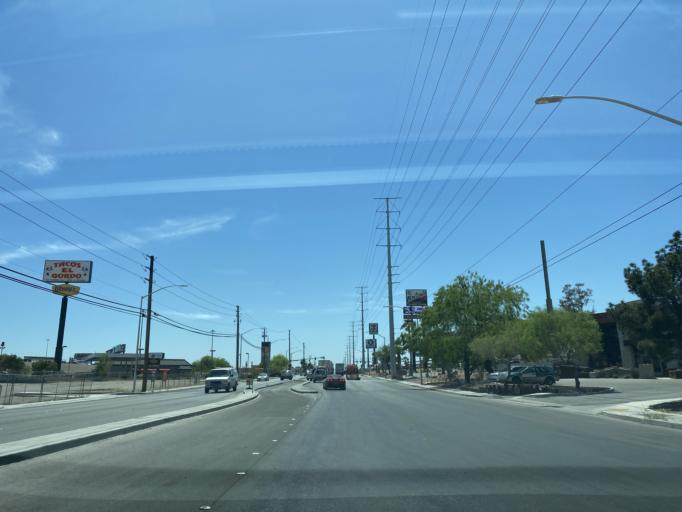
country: US
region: Nevada
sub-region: Clark County
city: North Las Vegas
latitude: 36.2200
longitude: -115.1256
